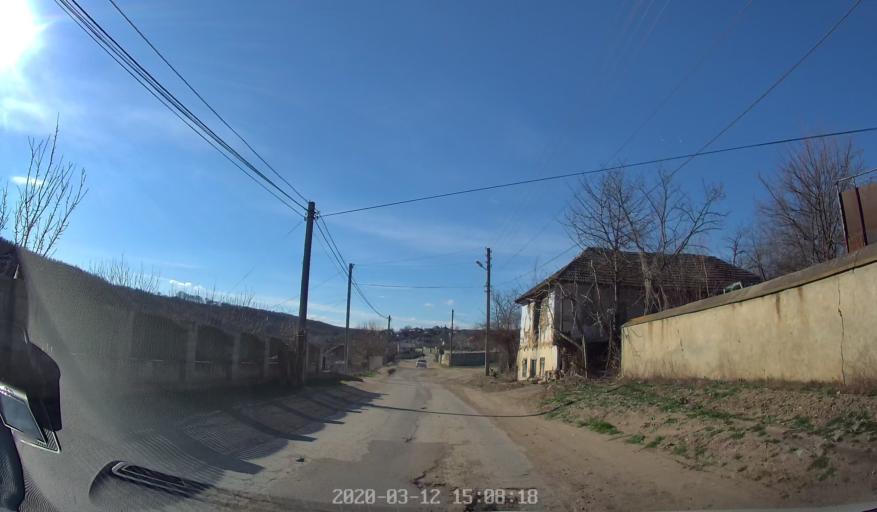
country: MD
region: Chisinau
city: Ciorescu
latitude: 47.2215
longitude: 28.9944
